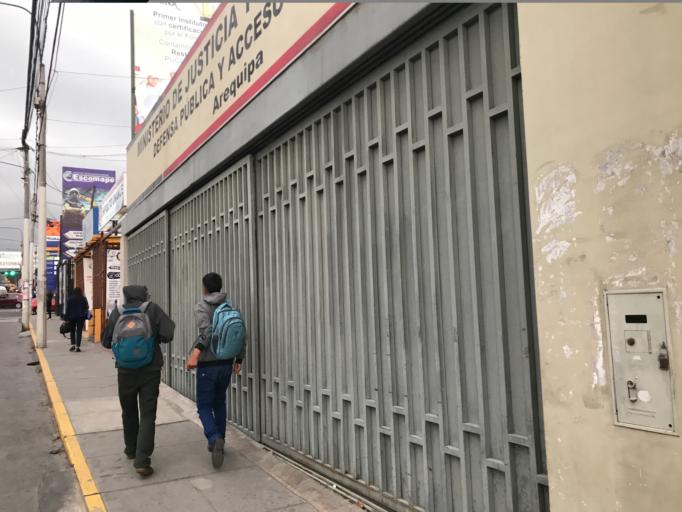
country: PE
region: Arequipa
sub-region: Provincia de Arequipa
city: Arequipa
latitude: -16.4052
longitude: -71.5284
